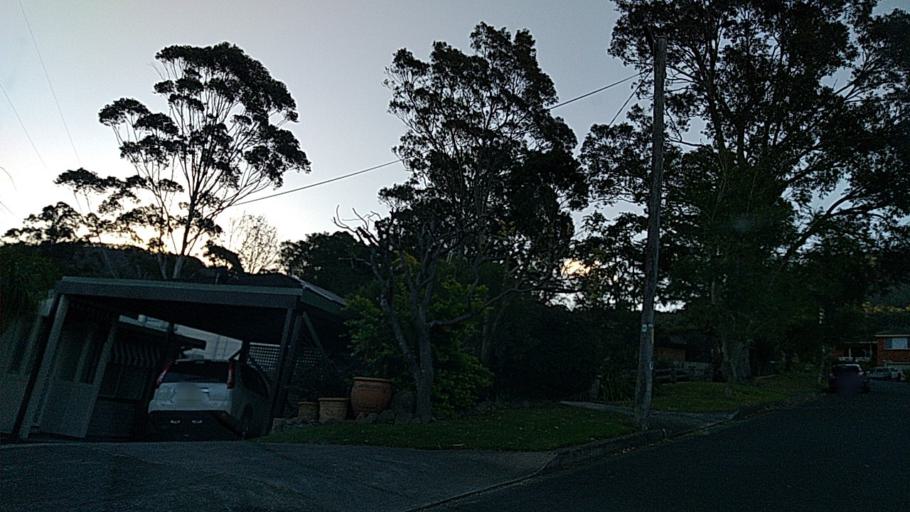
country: AU
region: New South Wales
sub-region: Wollongong
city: Mount Keira
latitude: -34.4176
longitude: 150.8555
